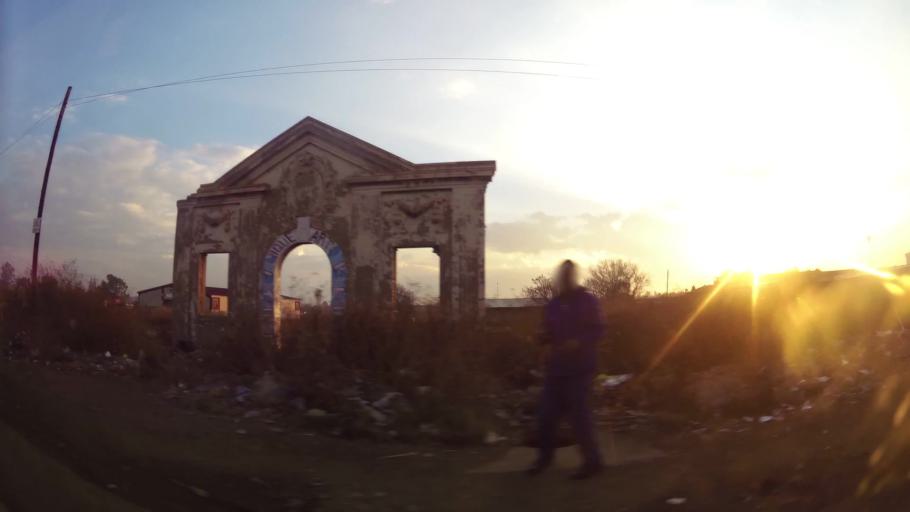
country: ZA
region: Gauteng
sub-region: City of Johannesburg Metropolitan Municipality
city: Orange Farm
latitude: -26.5360
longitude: 27.8856
